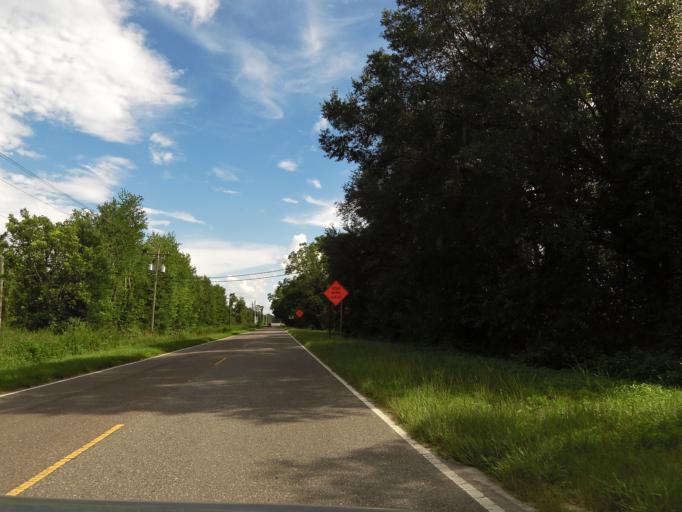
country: US
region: Florida
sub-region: Clay County
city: Green Cove Springs
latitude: 29.9565
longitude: -81.6937
